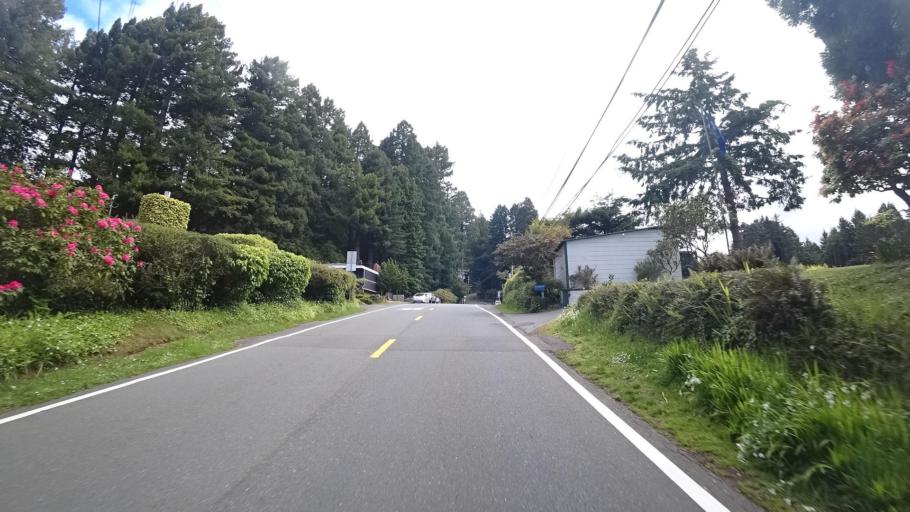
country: US
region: California
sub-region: Humboldt County
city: Arcata
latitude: 40.8679
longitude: -124.0720
